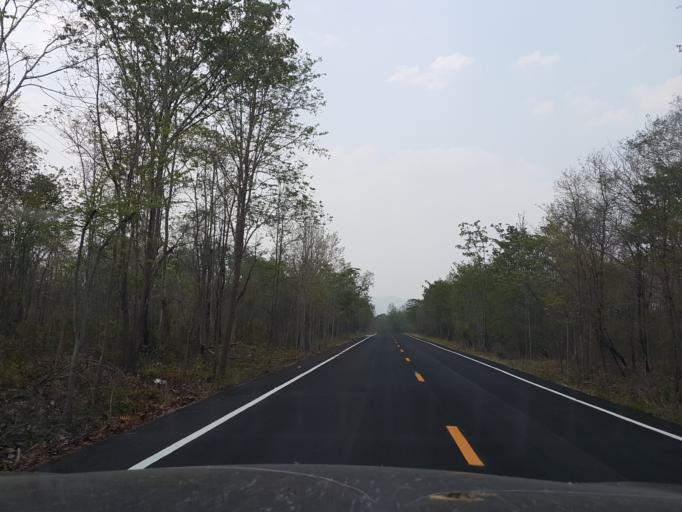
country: TH
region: Lampang
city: Mae Phrik
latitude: 17.4828
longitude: 99.1083
